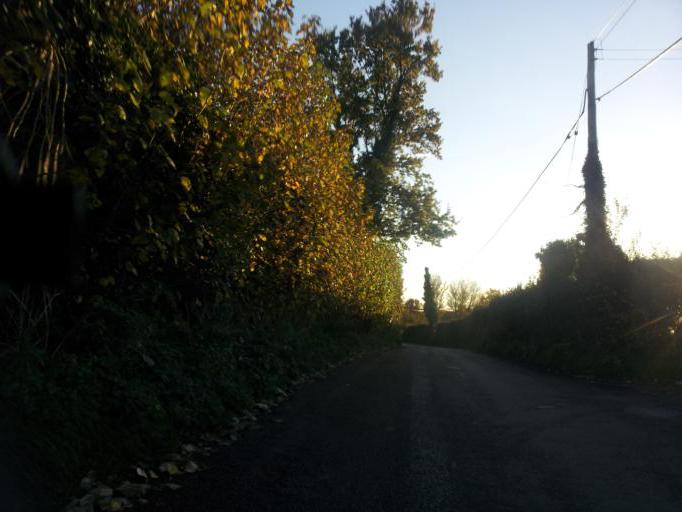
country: GB
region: England
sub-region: Kent
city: Newington
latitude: 51.3788
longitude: 0.6517
